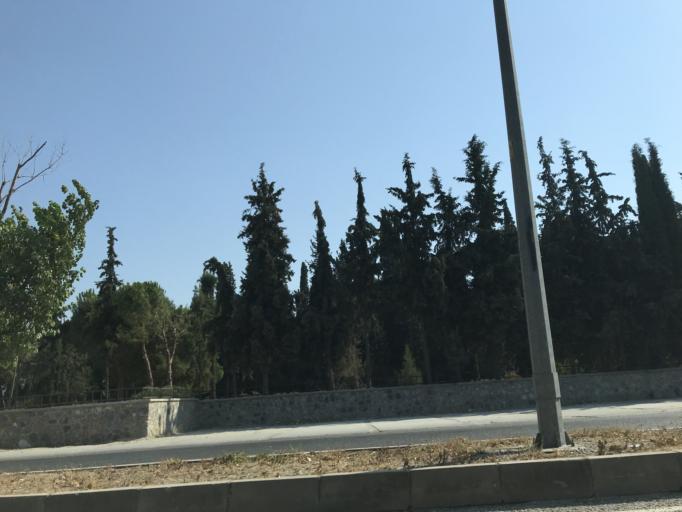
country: TR
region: Izmir
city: Selcuk
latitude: 37.9487
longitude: 27.3604
